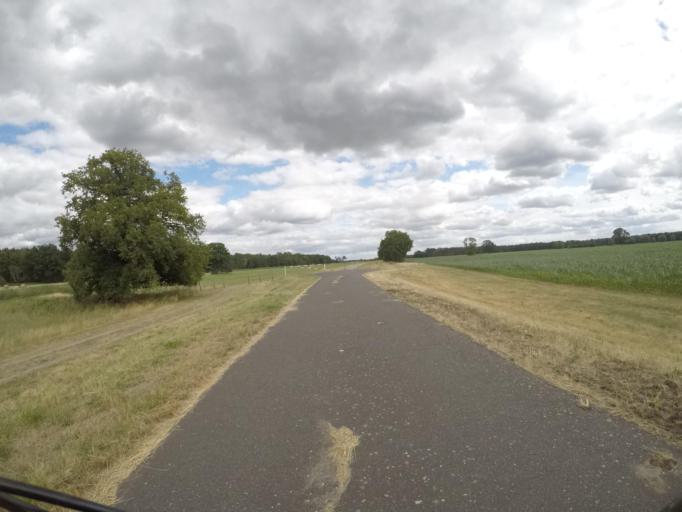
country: DE
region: Mecklenburg-Vorpommern
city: Lubtheen
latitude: 53.2965
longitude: 10.9816
